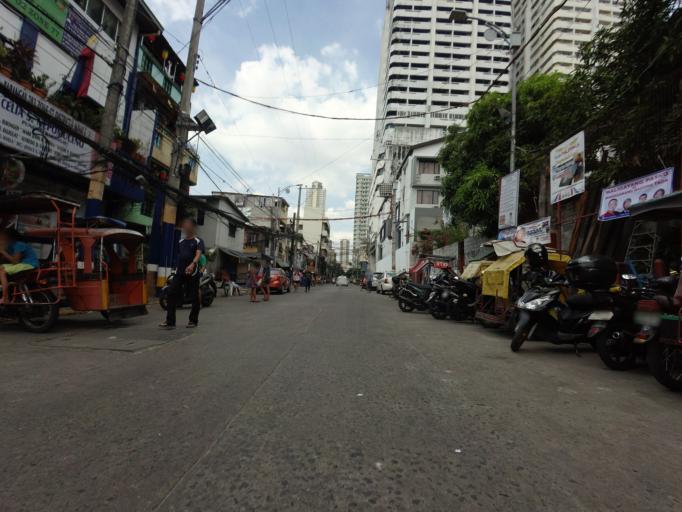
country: PH
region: Metro Manila
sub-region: City of Manila
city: Port Area
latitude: 14.5701
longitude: 120.9881
